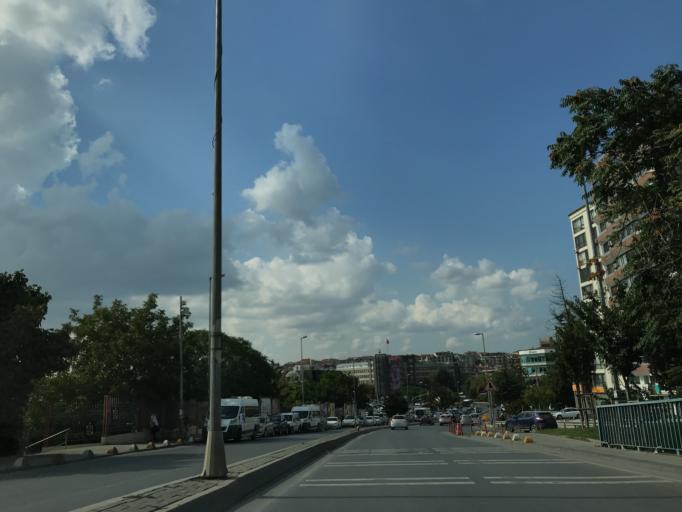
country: TR
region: Istanbul
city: UEskuedar
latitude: 40.9904
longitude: 29.0404
